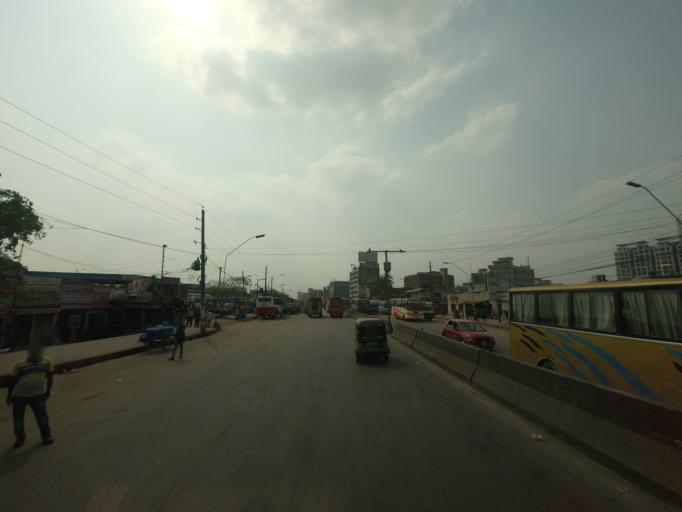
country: BD
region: Dhaka
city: Azimpur
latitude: 23.7832
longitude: 90.3449
